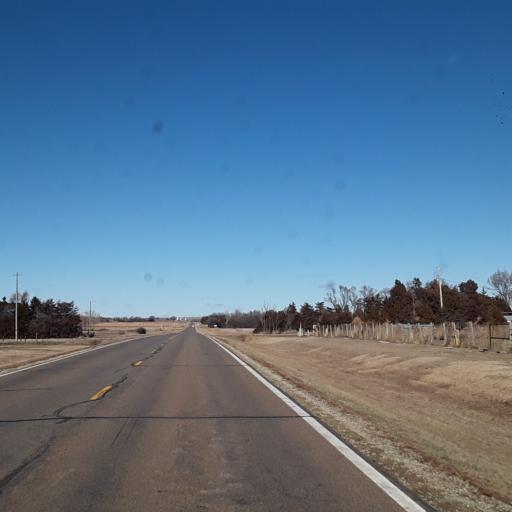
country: US
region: Kansas
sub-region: Lincoln County
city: Lincoln
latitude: 38.9777
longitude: -98.1513
